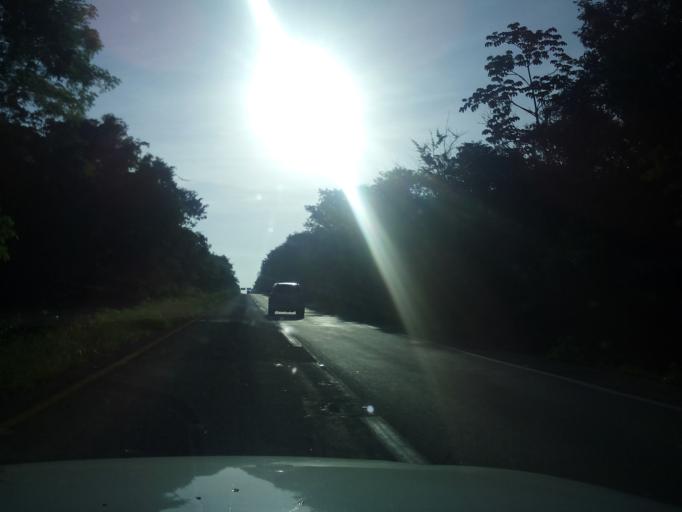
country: MX
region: Yucatan
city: Piste
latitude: 20.7331
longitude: -88.6023
